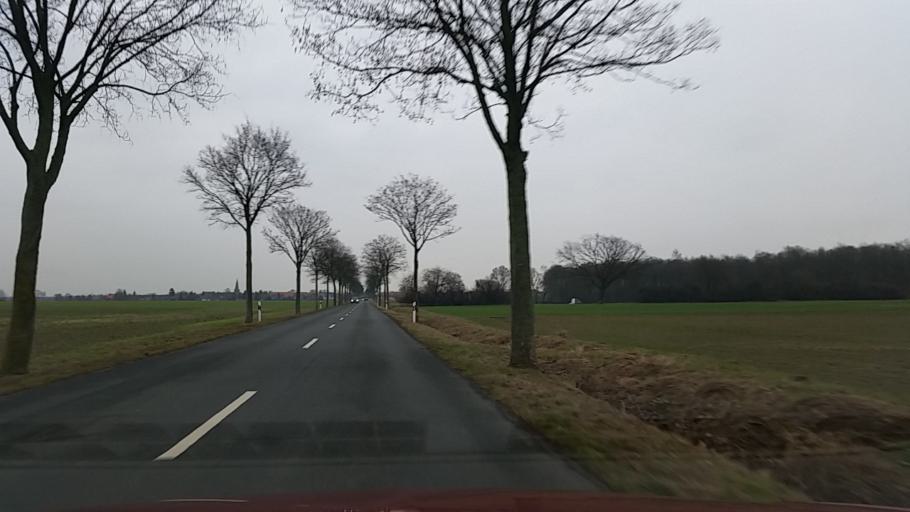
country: DE
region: Lower Saxony
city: Meine
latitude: 52.3592
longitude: 10.5733
